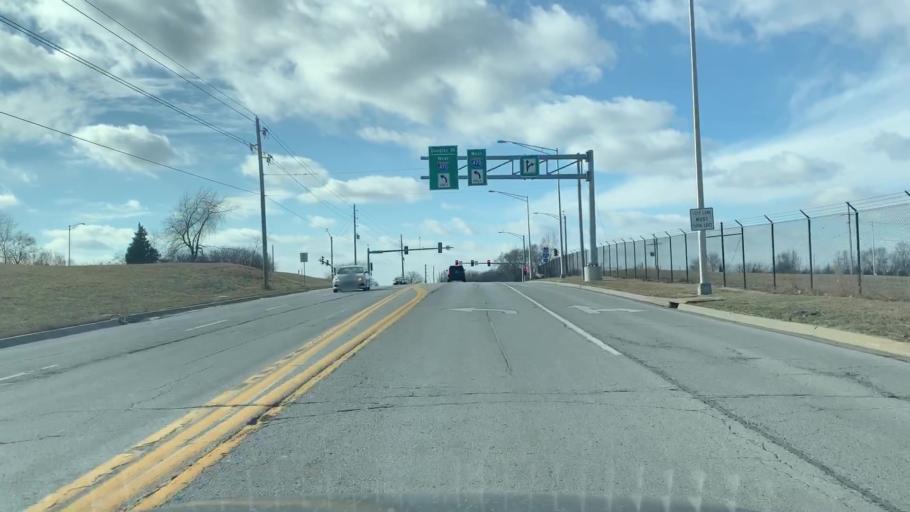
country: US
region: Missouri
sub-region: Jackson County
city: Lees Summit
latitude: 38.9466
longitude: -94.3766
